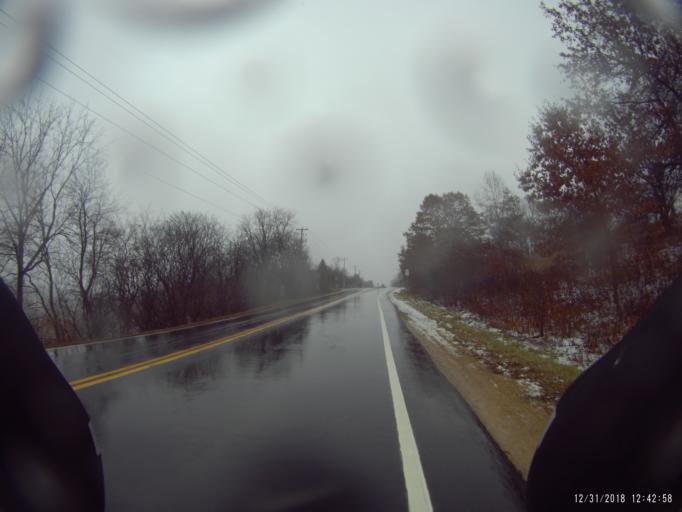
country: US
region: Wisconsin
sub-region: Dane County
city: Verona
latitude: 43.0296
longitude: -89.5103
